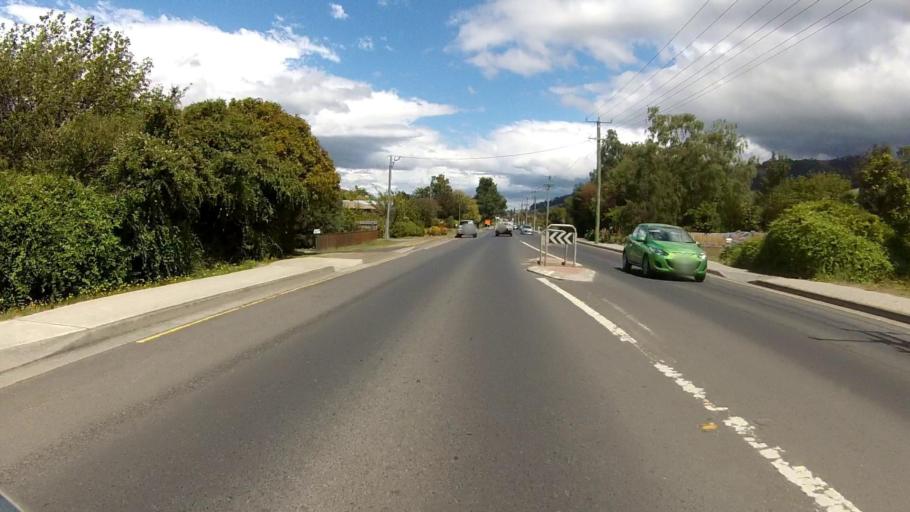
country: AU
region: Tasmania
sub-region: Huon Valley
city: Huonville
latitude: -43.0238
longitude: 147.0522
